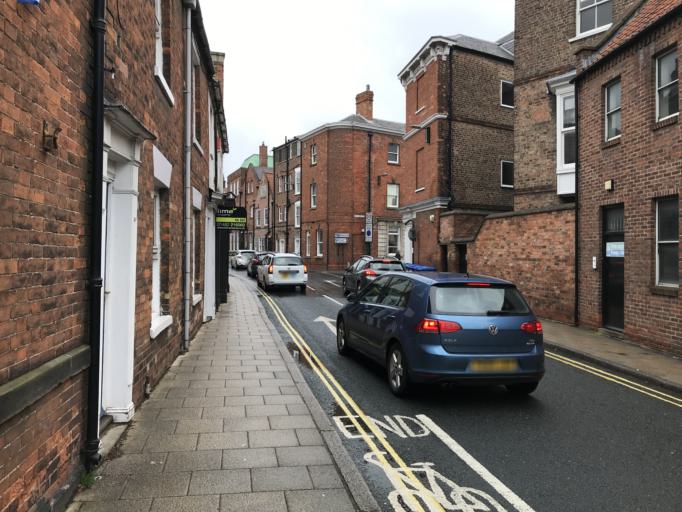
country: GB
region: England
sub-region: East Riding of Yorkshire
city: Beverley
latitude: 53.8427
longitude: -0.4331
